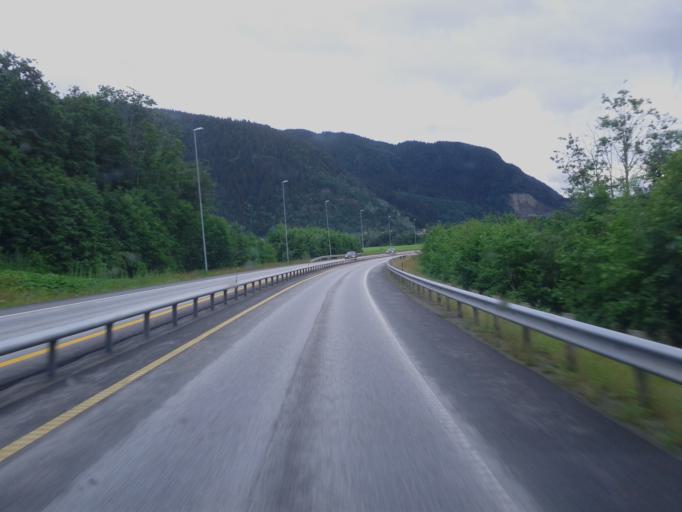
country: NO
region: Sor-Trondelag
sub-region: Melhus
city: Melhus
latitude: 63.2759
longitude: 10.2855
